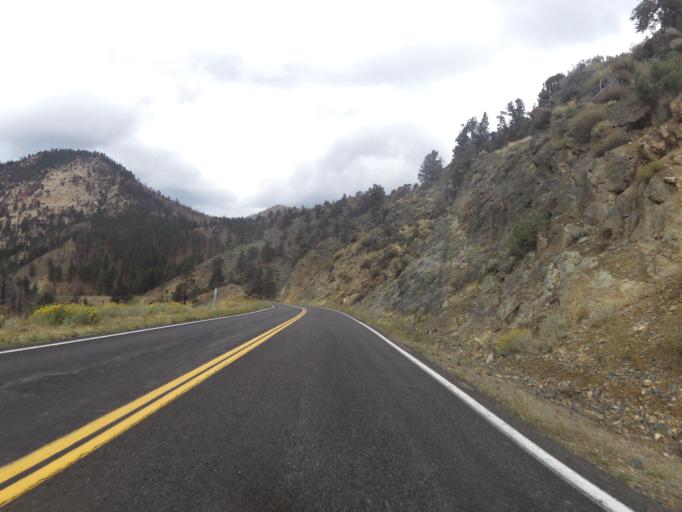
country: US
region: Nevada
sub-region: Douglas County
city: Gardnerville Ranchos
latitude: 38.6635
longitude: -119.6886
